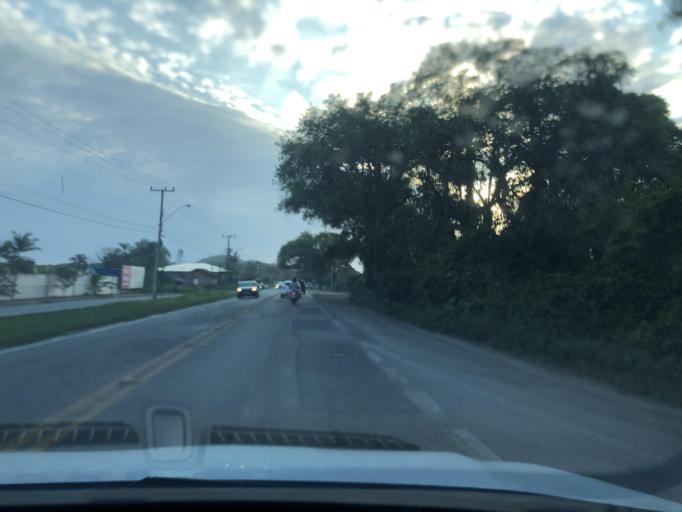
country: BR
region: Santa Catarina
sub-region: Sao Francisco Do Sul
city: Sao Francisco do Sul
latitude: -26.2478
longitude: -48.6056
